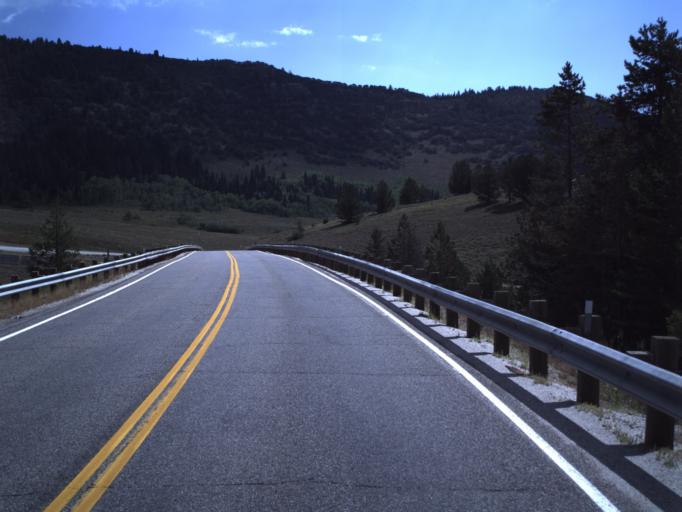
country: US
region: Idaho
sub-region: Bear Lake County
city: Paris
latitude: 41.9516
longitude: -111.4942
